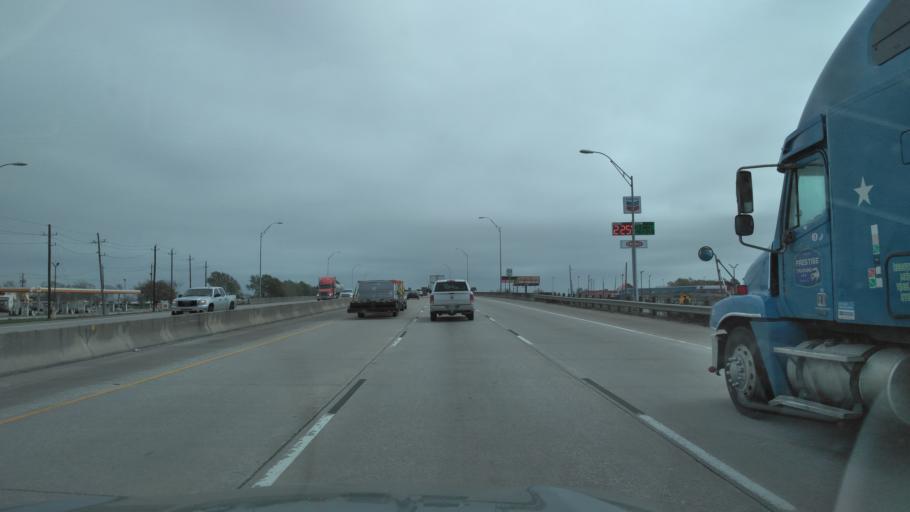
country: US
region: Texas
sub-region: Chambers County
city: Old River-Winfree
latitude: 29.8293
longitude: -94.8055
